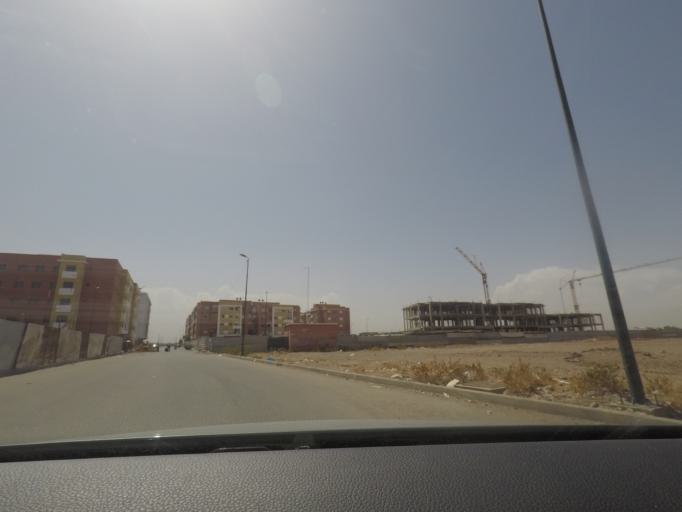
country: MA
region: Marrakech-Tensift-Al Haouz
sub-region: Marrakech
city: Marrakesh
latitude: 31.5871
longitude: -8.0396
